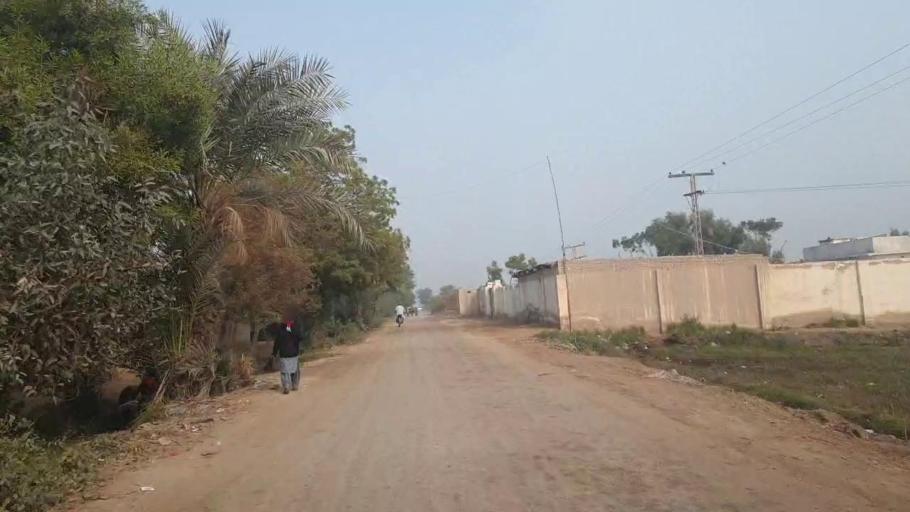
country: PK
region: Sindh
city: Tando Adam
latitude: 25.7896
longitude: 68.6103
